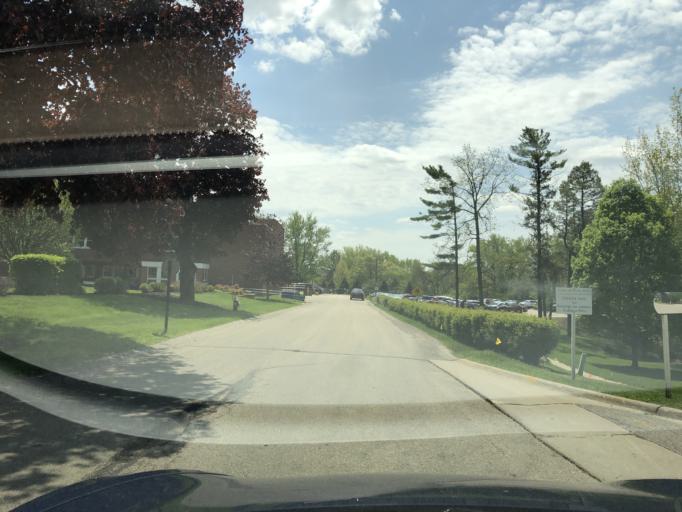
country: US
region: Illinois
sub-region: Jo Daviess County
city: East Dubuque
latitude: 42.4772
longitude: -90.6585
